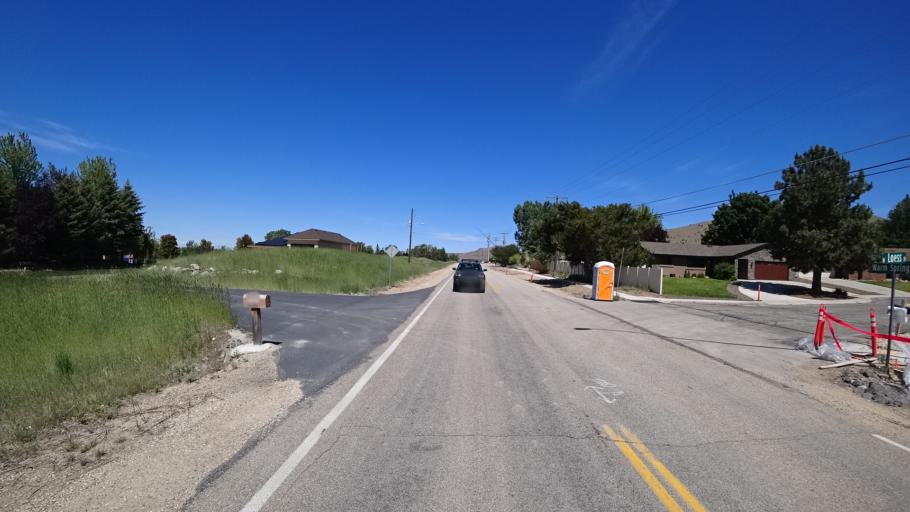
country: US
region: Idaho
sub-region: Ada County
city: Boise
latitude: 43.5589
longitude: -116.1010
